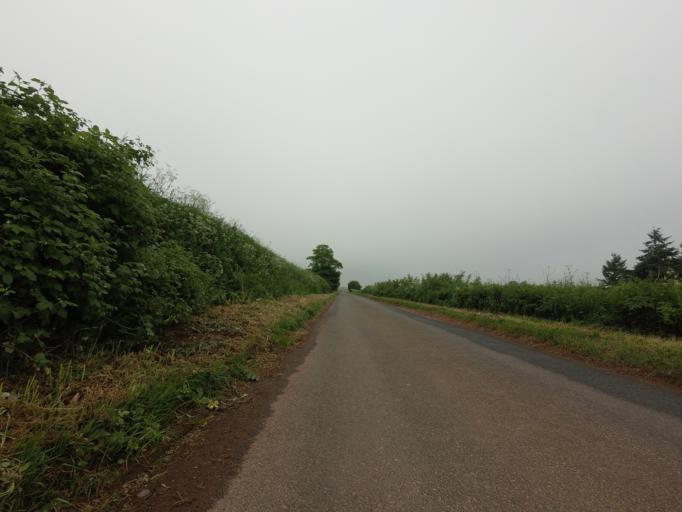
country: GB
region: Scotland
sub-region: Perth and Kinross
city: Abernethy
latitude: 56.2675
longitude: -3.2971
